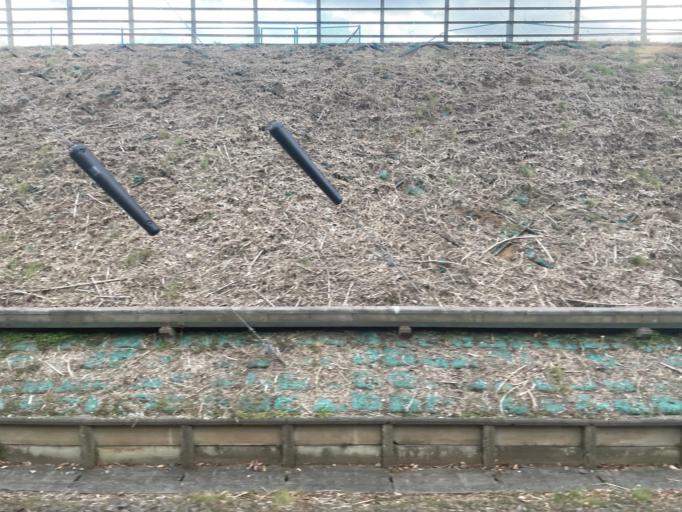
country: JP
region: Tokyo
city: Hachioji
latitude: 35.6455
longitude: 139.3325
